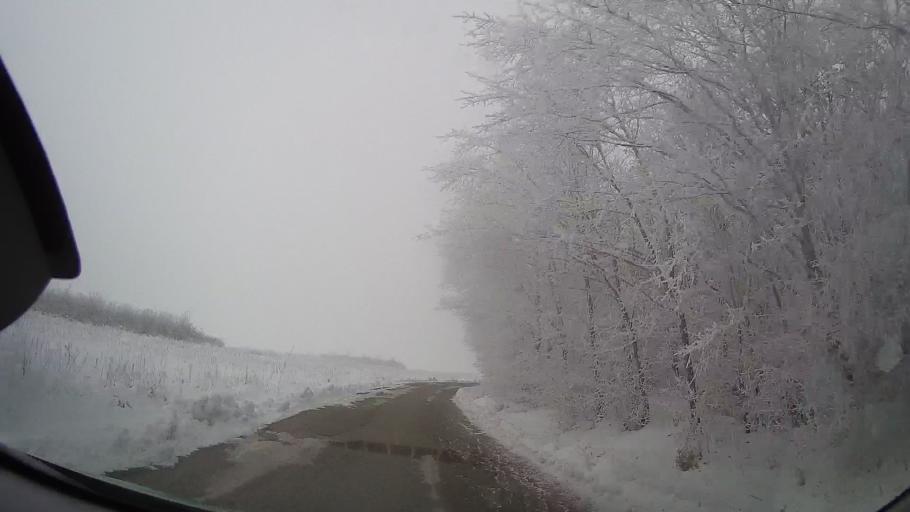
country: RO
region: Iasi
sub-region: Comuna Dagata
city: Dagata
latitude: 46.9166
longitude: 27.1810
